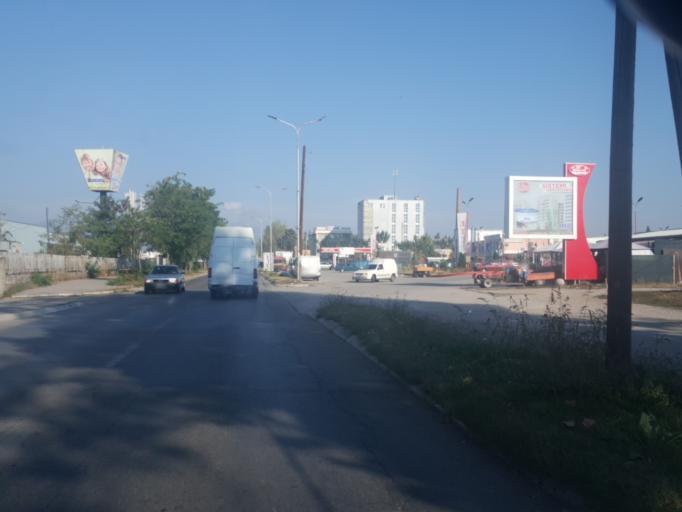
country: XK
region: Gjakova
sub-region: Komuna e Gjakoves
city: Gjakove
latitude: 42.3935
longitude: 20.4227
